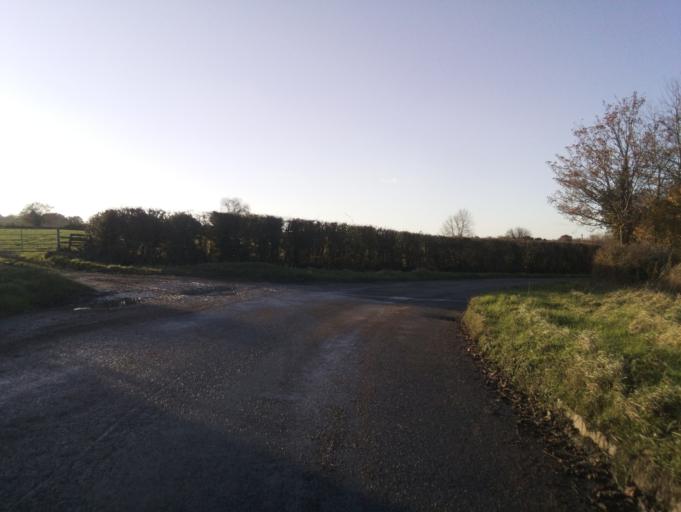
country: GB
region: England
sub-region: Somerset
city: Milborne Port
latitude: 51.0076
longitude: -2.4337
